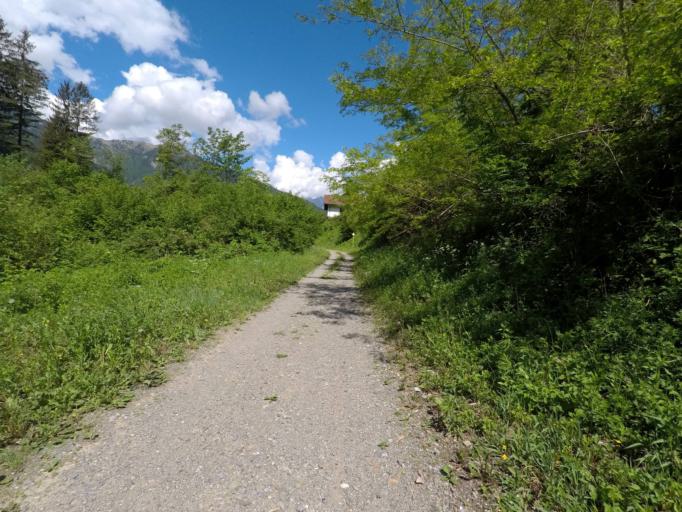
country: IT
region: Friuli Venezia Giulia
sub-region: Provincia di Udine
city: Ovaro
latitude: 46.4670
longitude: 12.8762
